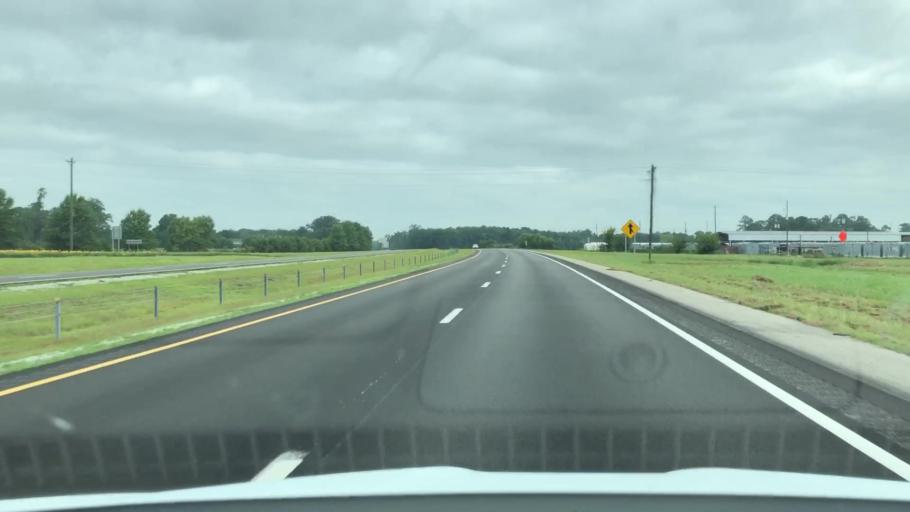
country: US
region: North Carolina
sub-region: Wayne County
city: Fremont
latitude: 35.5504
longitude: -77.9872
